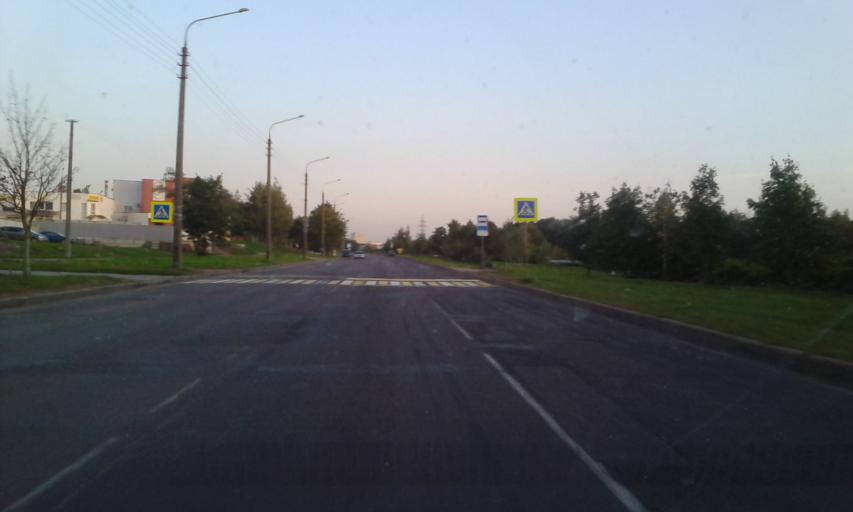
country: BY
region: Minsk
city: Vyaliki Trastsyanets
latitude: 53.8380
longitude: 27.6776
